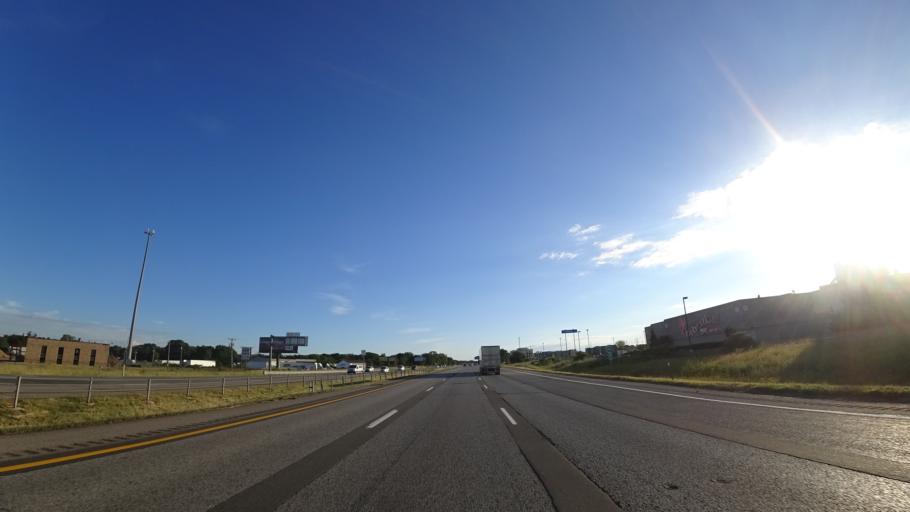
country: US
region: Michigan
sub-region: Berrien County
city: Fair Plain
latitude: 42.0761
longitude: -86.4214
